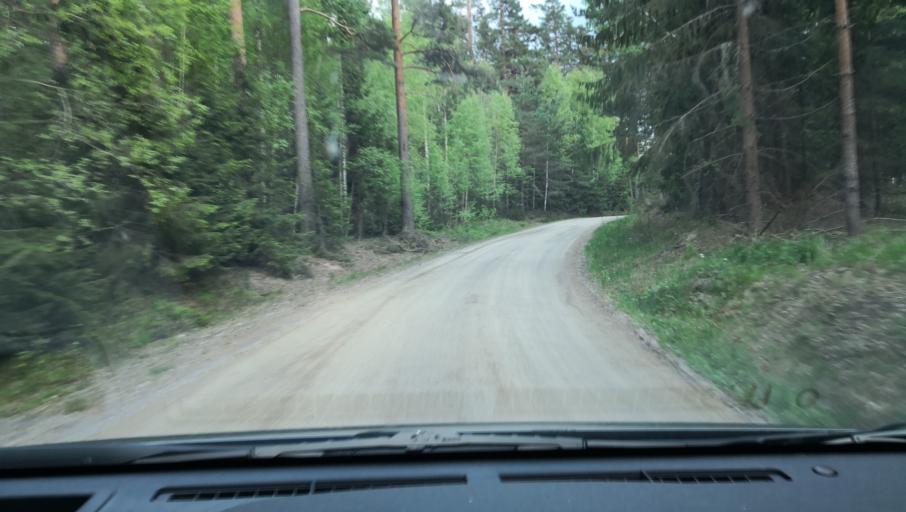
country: SE
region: Vaestmanland
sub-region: Skinnskattebergs Kommun
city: Skinnskatteberg
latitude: 59.7344
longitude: 15.4723
